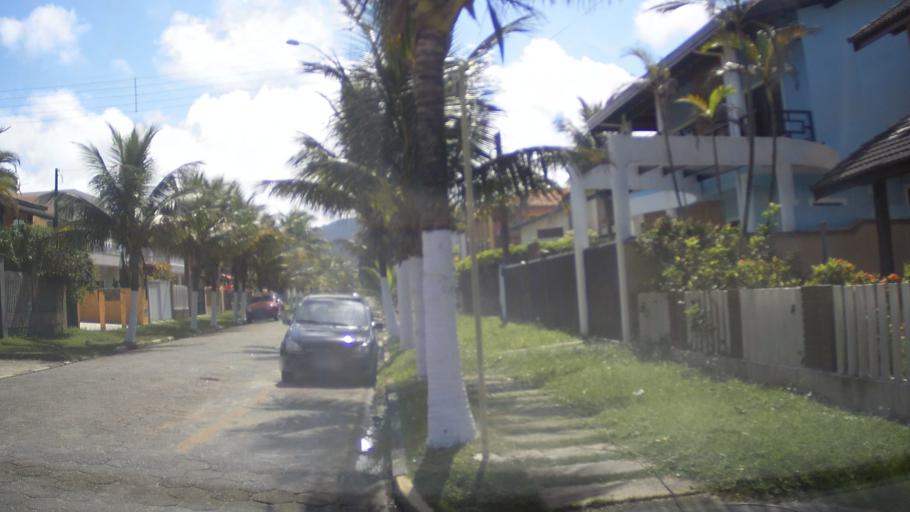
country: BR
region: Sao Paulo
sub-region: Itanhaem
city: Itanhaem
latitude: -24.1492
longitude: -46.7207
